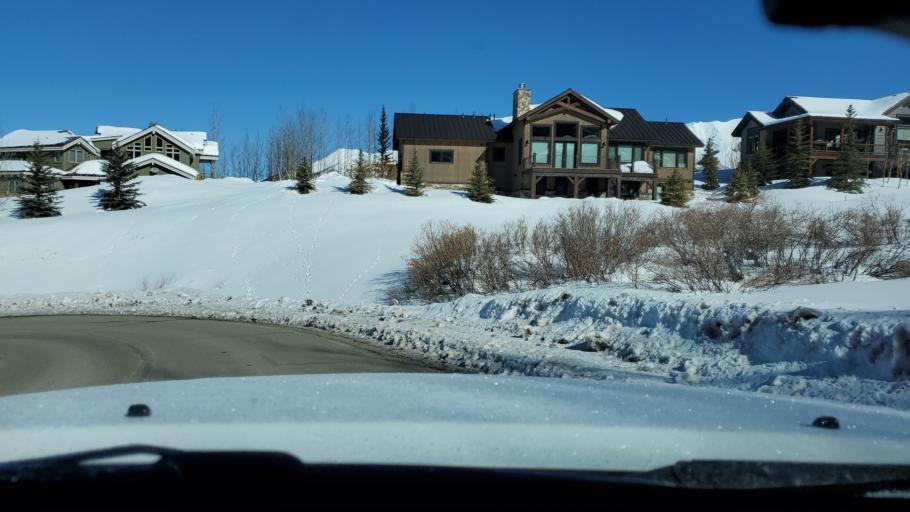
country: US
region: Colorado
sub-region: Gunnison County
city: Crested Butte
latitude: 38.9128
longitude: -106.9613
